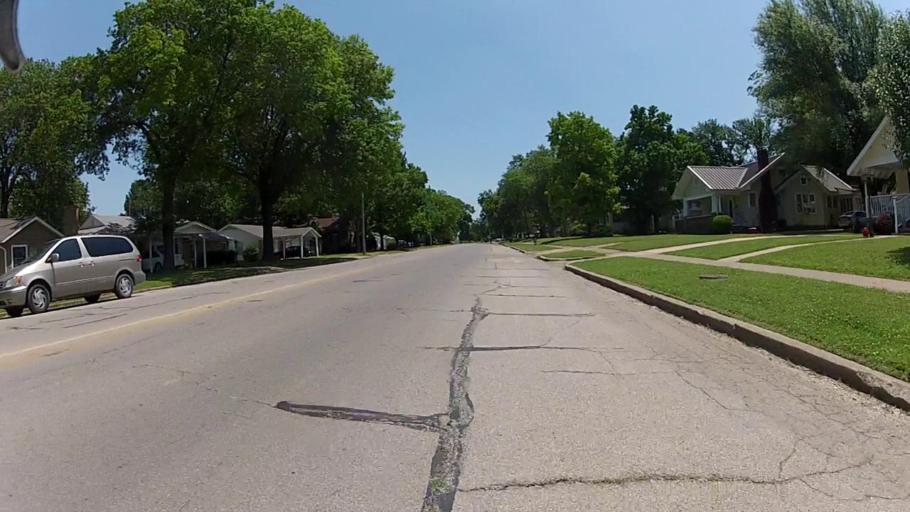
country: US
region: Kansas
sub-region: Montgomery County
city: Cherryvale
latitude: 37.2684
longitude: -95.5395
